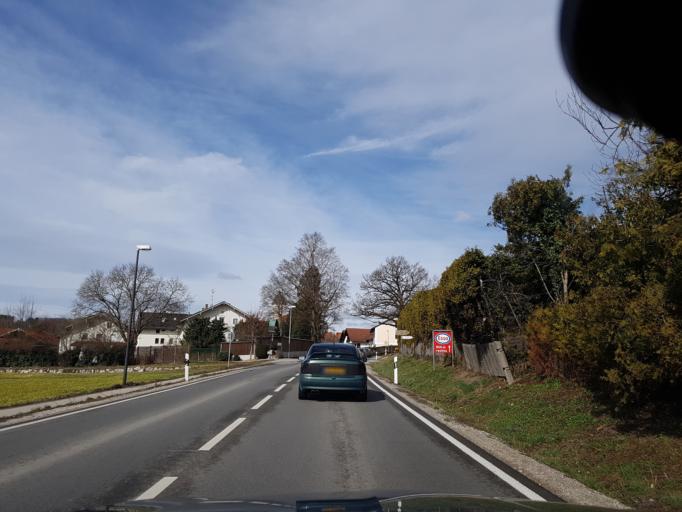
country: DE
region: Bavaria
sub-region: Upper Bavaria
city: Feldkirchen-Westerham
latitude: 47.9079
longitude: 11.8499
